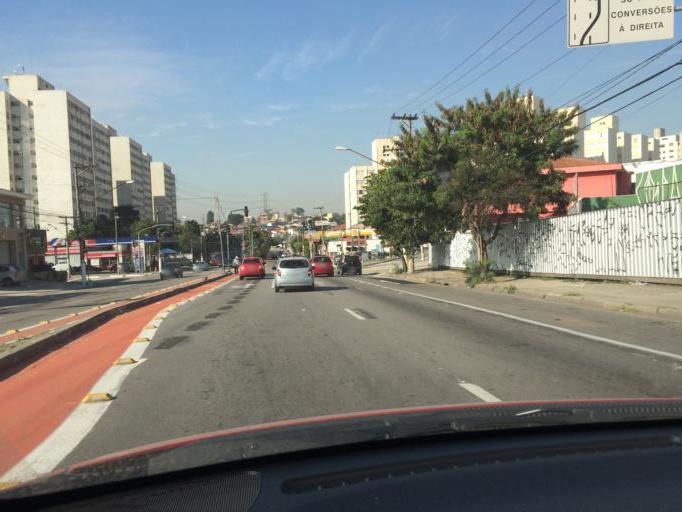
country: BR
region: Sao Paulo
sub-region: Osasco
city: Osasco
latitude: -23.5523
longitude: -46.7574
